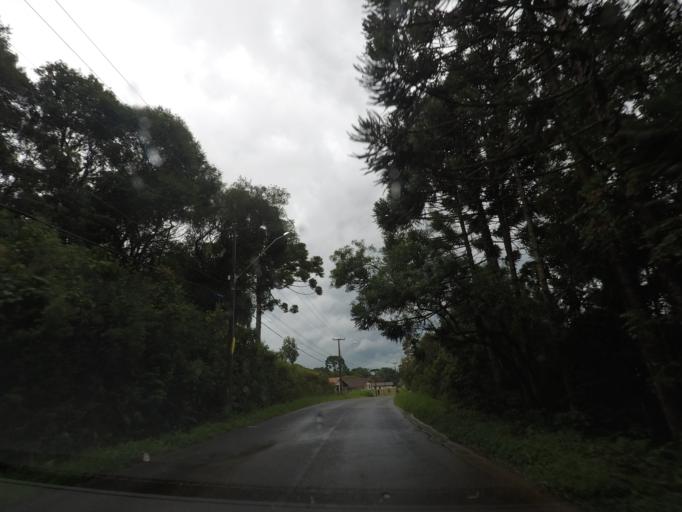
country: BR
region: Parana
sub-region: Campo Largo
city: Campo Largo
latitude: -25.4514
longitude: -49.4544
